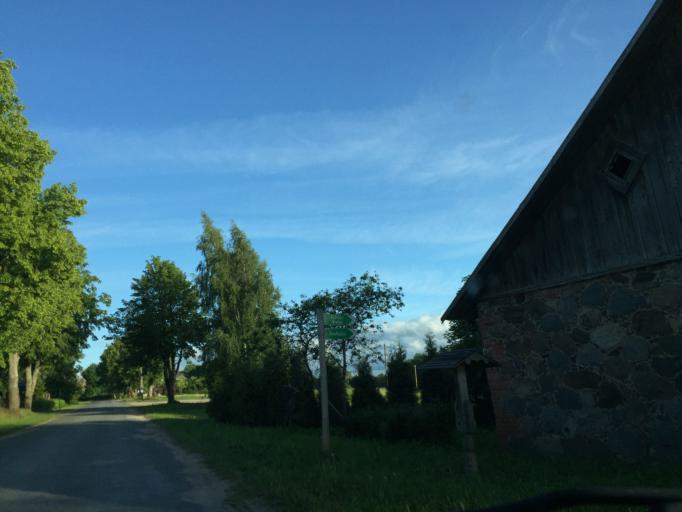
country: LV
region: Koceni
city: Koceni
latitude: 57.4785
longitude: 25.2398
